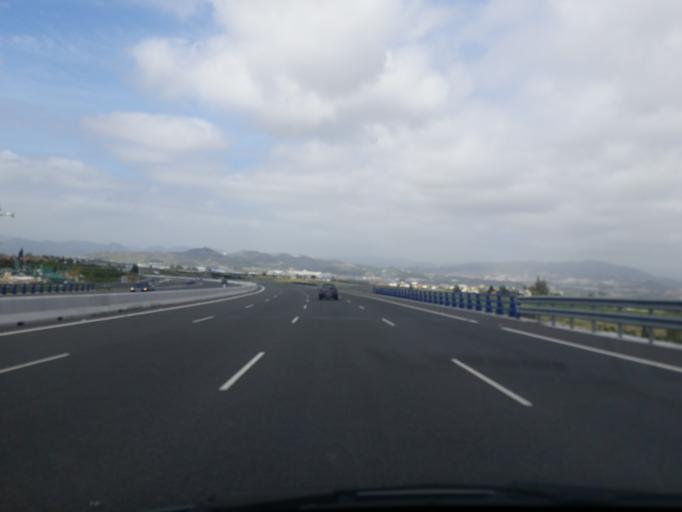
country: ES
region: Andalusia
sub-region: Provincia de Malaga
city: Alhaurin de la Torre
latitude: 36.6762
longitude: -4.5262
